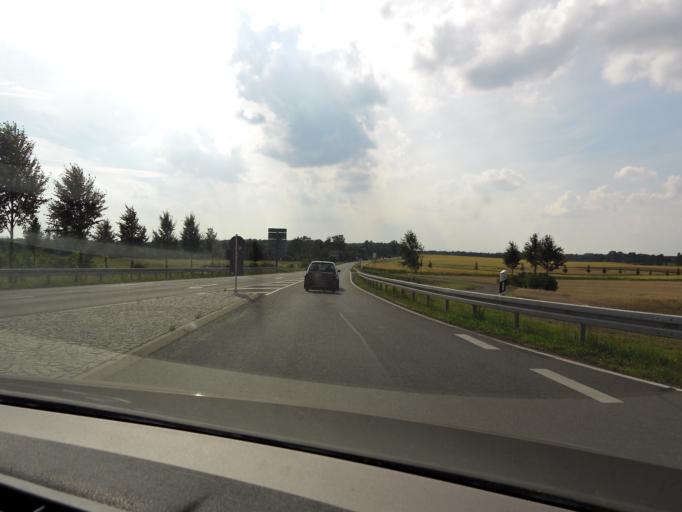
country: DE
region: Saxony
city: Grimma
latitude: 51.2321
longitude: 12.6974
